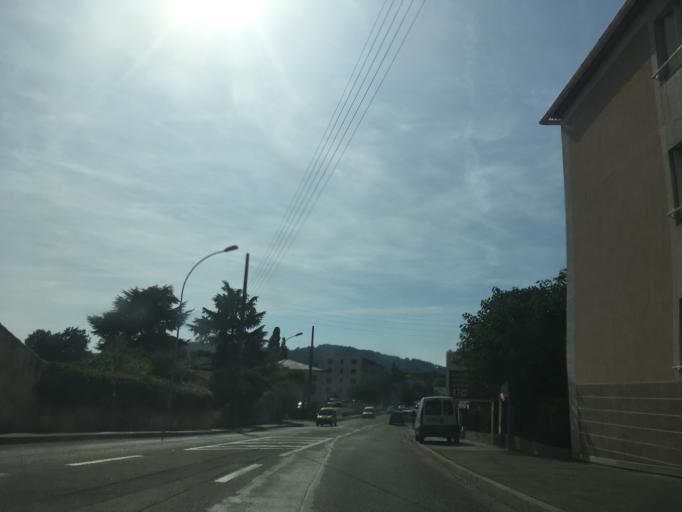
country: FR
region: Provence-Alpes-Cote d'Azur
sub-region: Departement du Var
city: Draguignan
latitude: 43.5313
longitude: 6.4736
